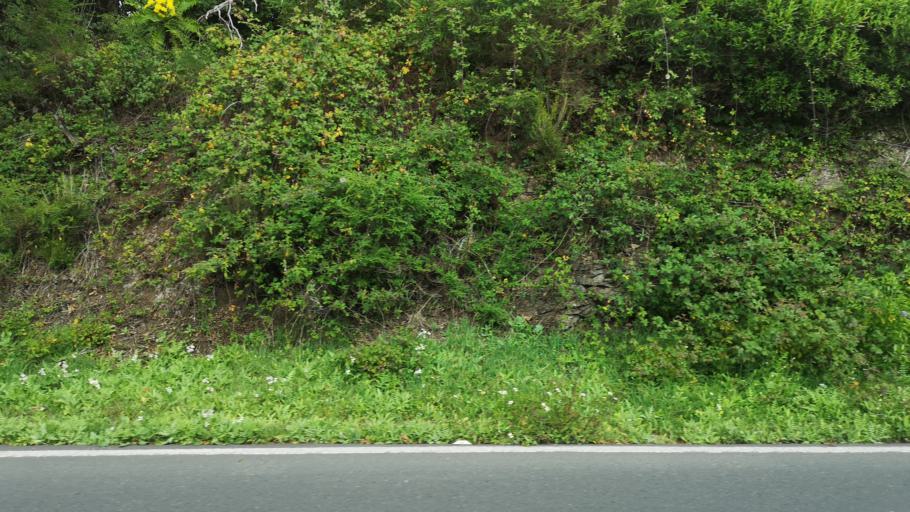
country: ES
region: Canary Islands
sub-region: Provincia de Santa Cruz de Tenerife
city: Alajero
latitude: 28.1090
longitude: -17.2264
